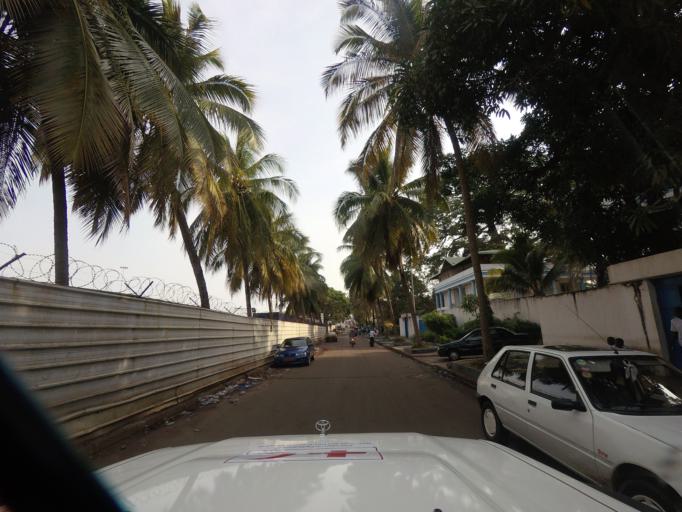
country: GN
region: Conakry
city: Camayenne
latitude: 9.5079
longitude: -13.7192
